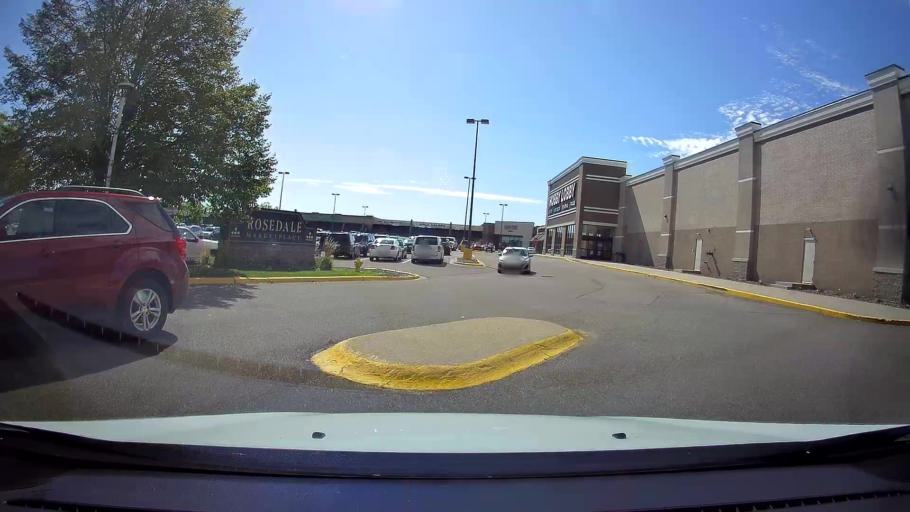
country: US
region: Minnesota
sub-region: Ramsey County
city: Roseville
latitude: 45.0146
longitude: -93.1797
